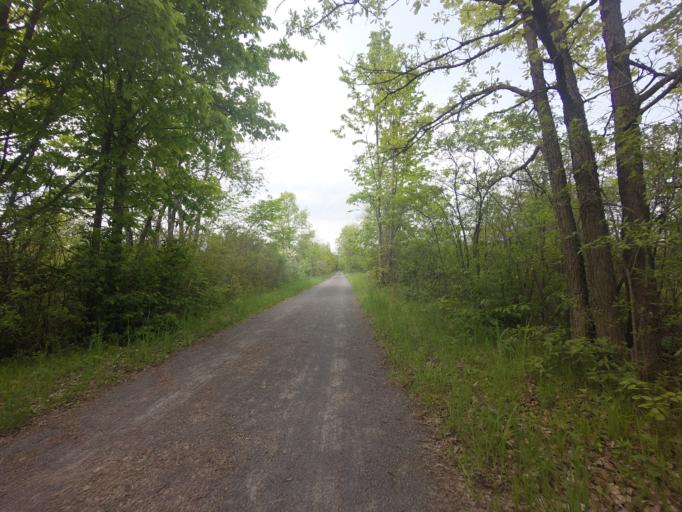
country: CA
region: Ontario
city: Kingston
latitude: 44.3250
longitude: -76.5882
